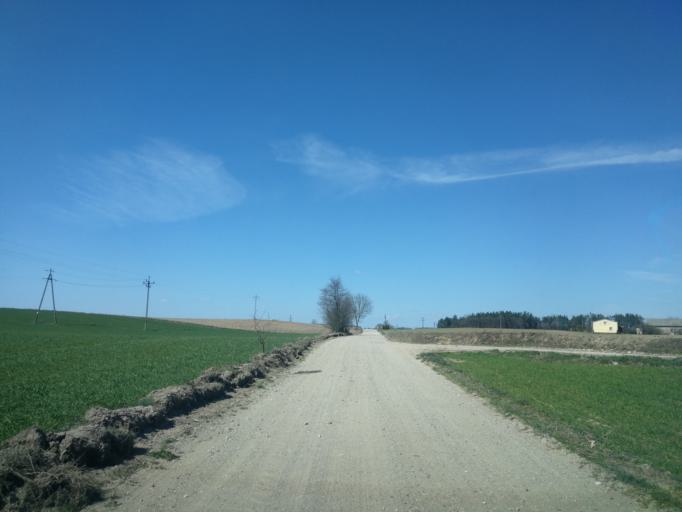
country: PL
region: Warmian-Masurian Voivodeship
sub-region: Powiat dzialdowski
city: Rybno
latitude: 53.4415
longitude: 19.9359
